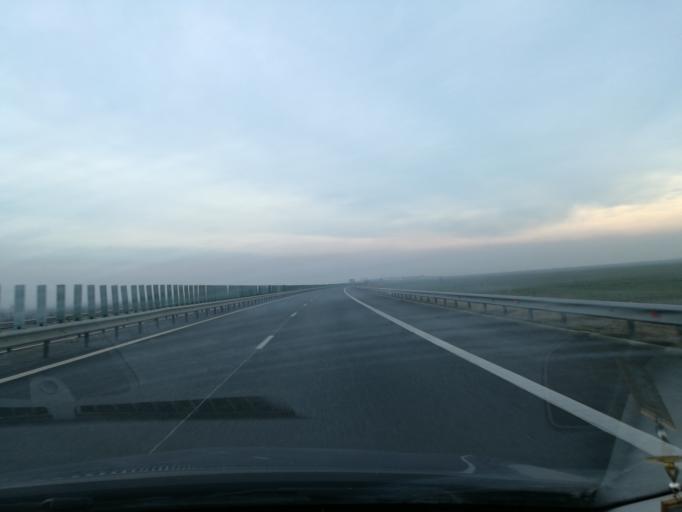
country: RO
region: Ialomita
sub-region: Municipiul Fetesti
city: Fetesti-Gara
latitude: 44.4148
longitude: 27.7742
